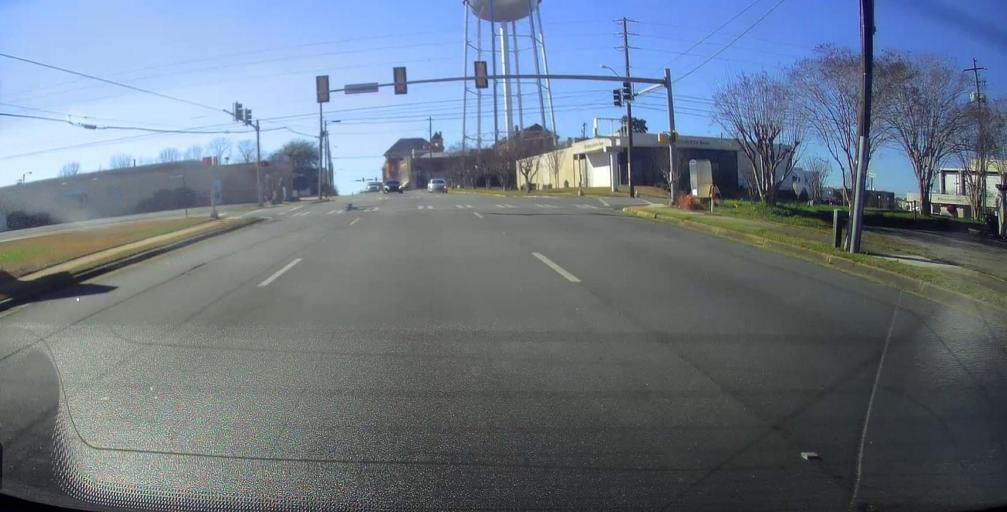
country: US
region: Georgia
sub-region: Sumter County
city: Americus
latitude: 32.0722
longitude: -84.2304
